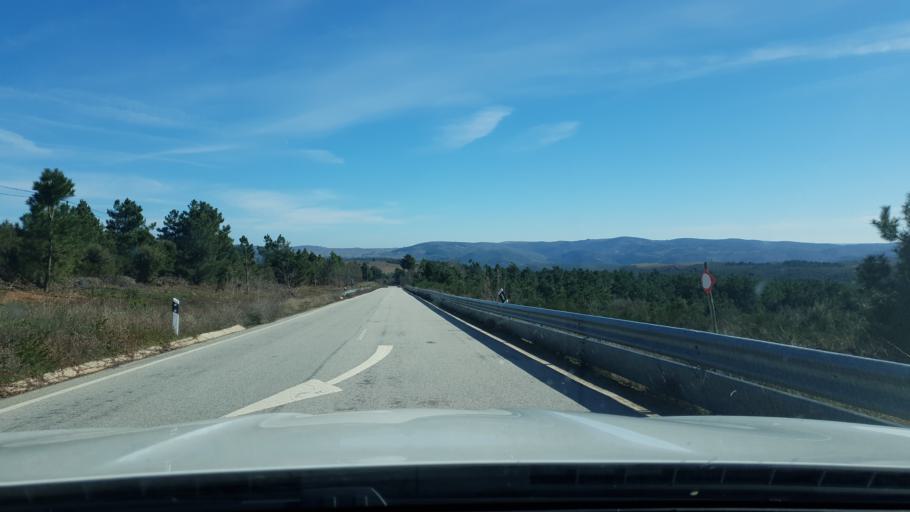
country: PT
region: Braganca
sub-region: Torre de Moncorvo
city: Torre de Moncorvo
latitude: 41.1788
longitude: -6.9221
